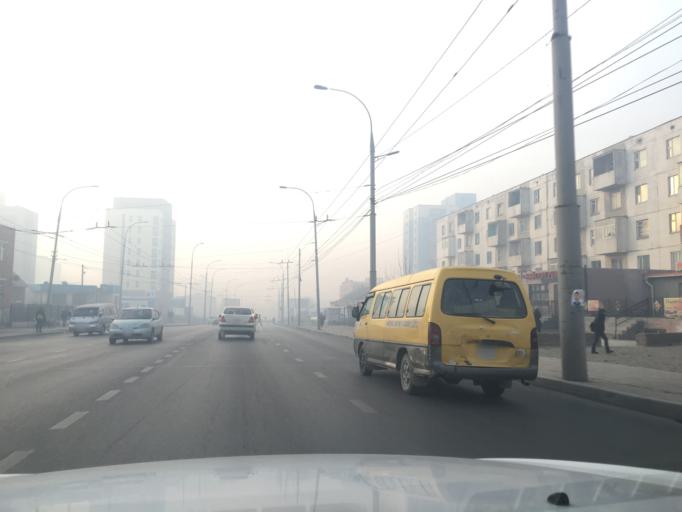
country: MN
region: Ulaanbaatar
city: Ulaanbaatar
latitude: 47.9170
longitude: 106.8182
